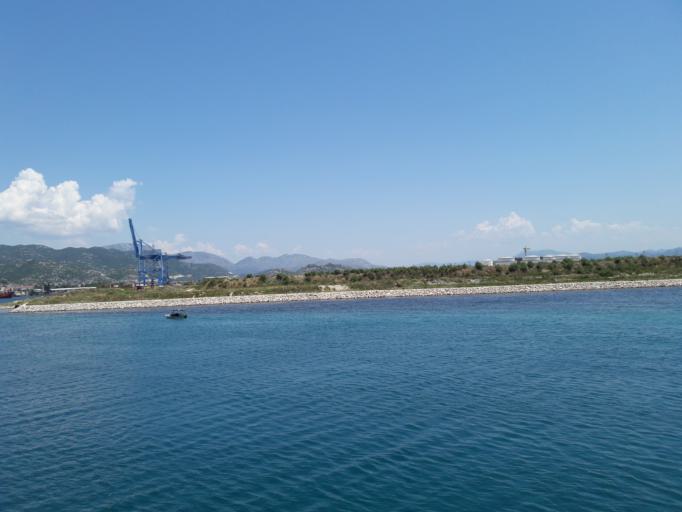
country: HR
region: Dubrovacko-Neretvanska
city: Komin
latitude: 43.0416
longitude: 17.4200
